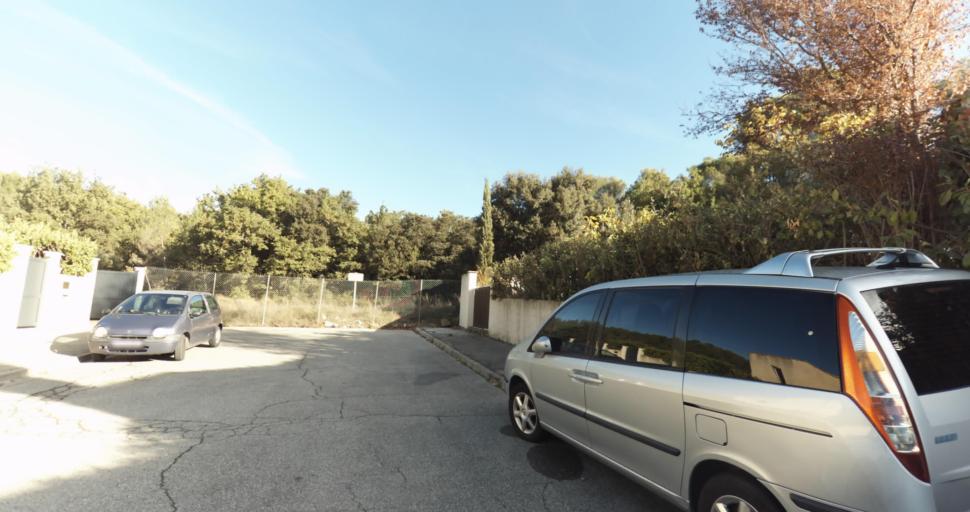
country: FR
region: Provence-Alpes-Cote d'Azur
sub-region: Departement des Bouches-du-Rhone
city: Venelles
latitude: 43.5971
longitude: 5.4719
